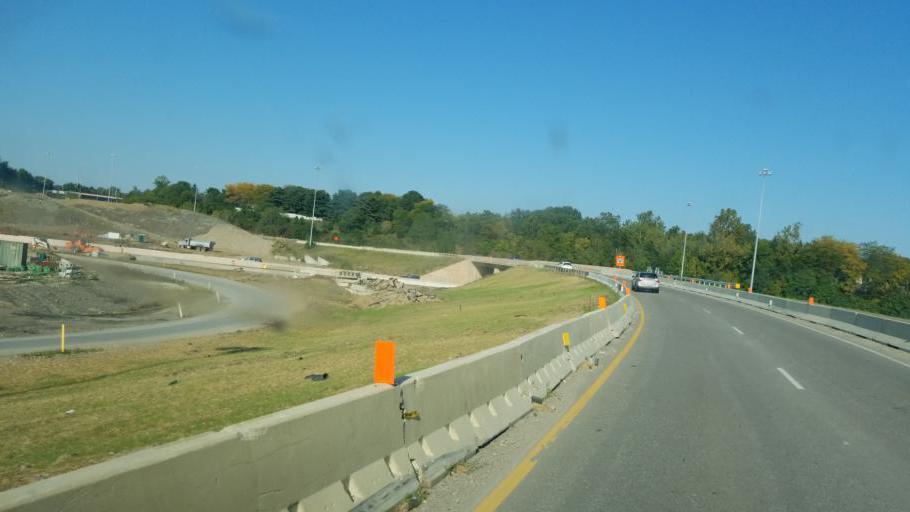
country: US
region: Ohio
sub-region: Franklin County
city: Worthington
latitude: 40.1136
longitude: -83.0332
